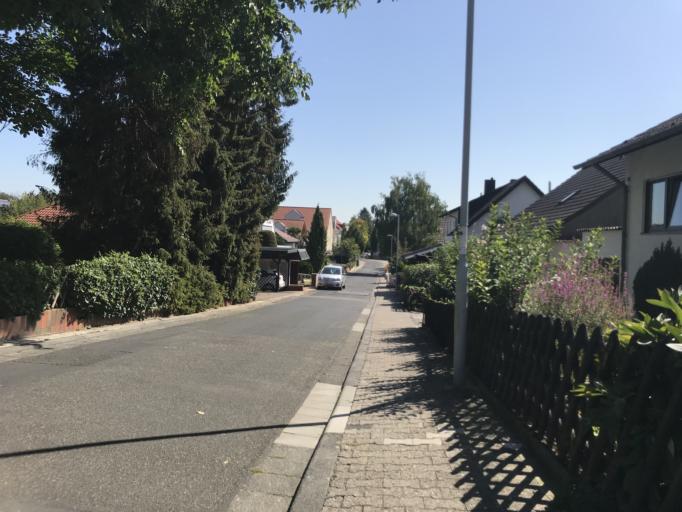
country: DE
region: Rheinland-Pfalz
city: Bodenheim
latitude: 49.9577
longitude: 8.3097
